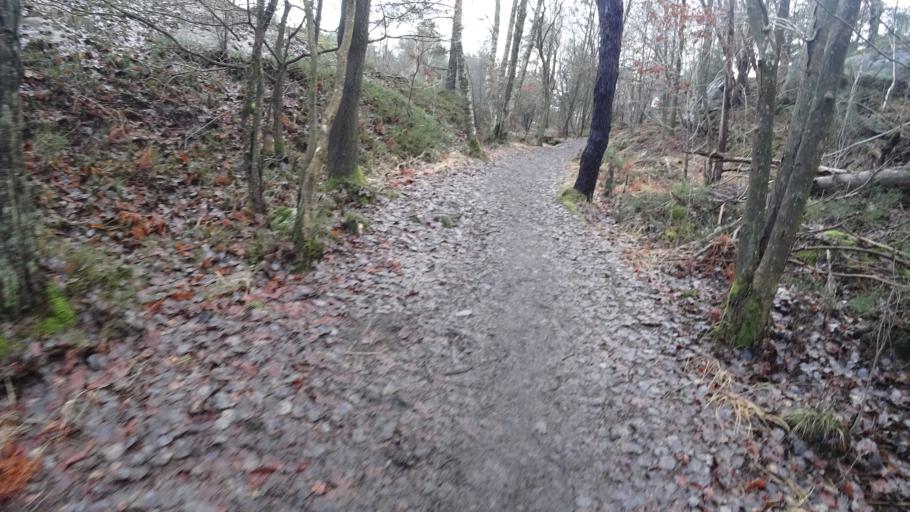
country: SE
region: Vaestra Goetaland
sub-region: Goteborg
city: Goeteborg
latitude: 57.6678
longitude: 11.9552
